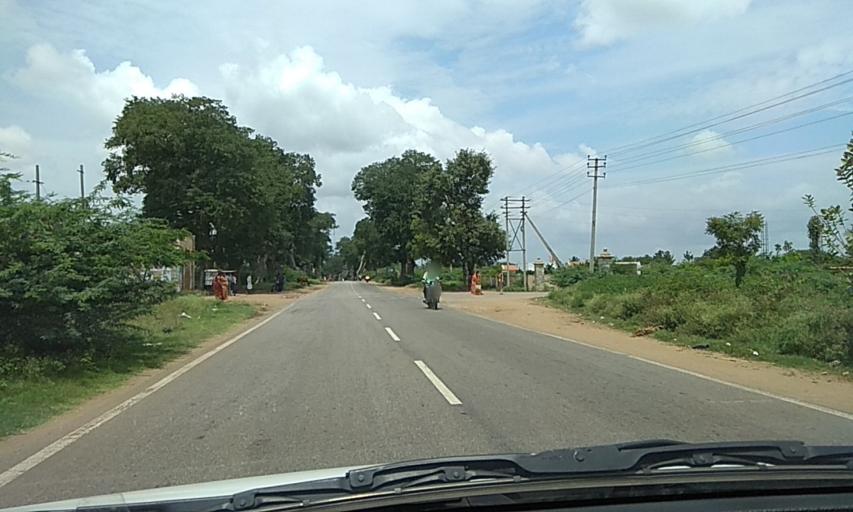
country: IN
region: Karnataka
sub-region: Chamrajnagar
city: Gundlupet
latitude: 11.8107
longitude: 76.7170
